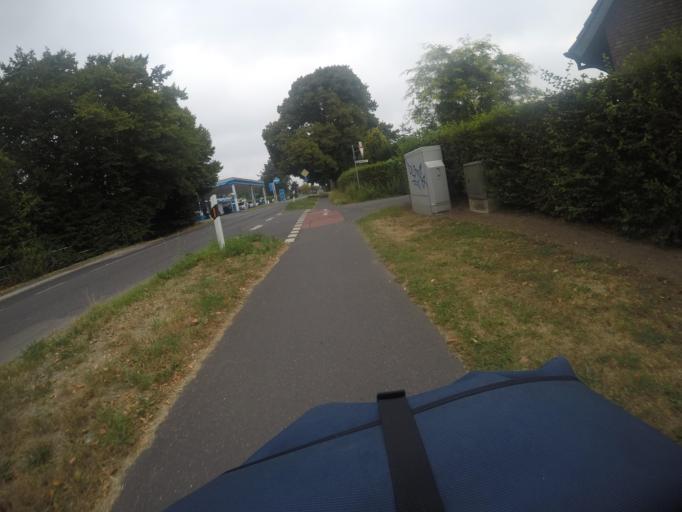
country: DE
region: North Rhine-Westphalia
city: Tonisvorst
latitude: 51.3822
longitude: 6.5054
